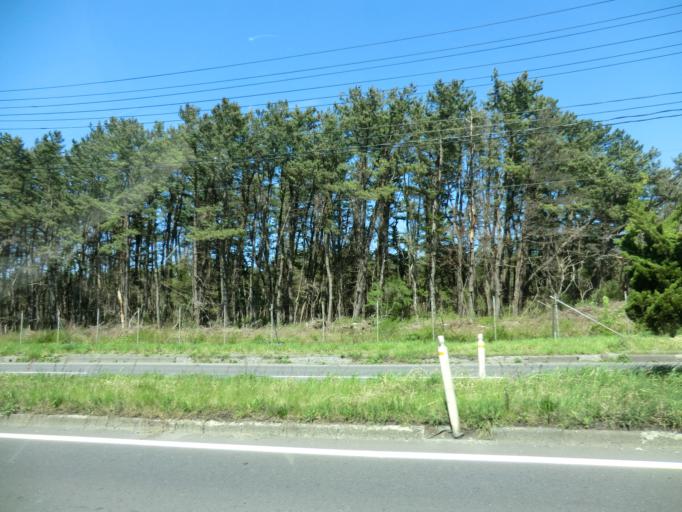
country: JP
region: Aomori
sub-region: Hachinohe Shi
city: Uchimaru
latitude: 40.5762
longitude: 141.4711
